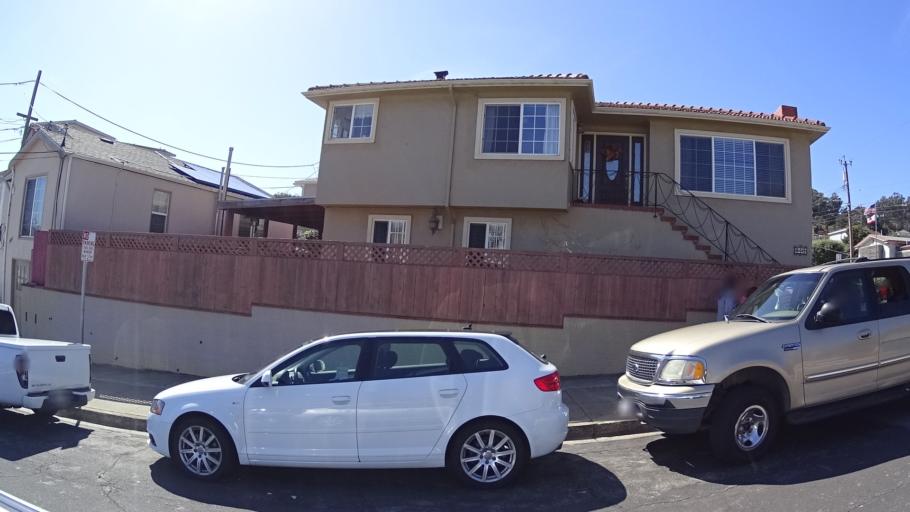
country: US
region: California
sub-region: San Mateo County
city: South San Francisco
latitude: 37.6629
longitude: -122.4093
